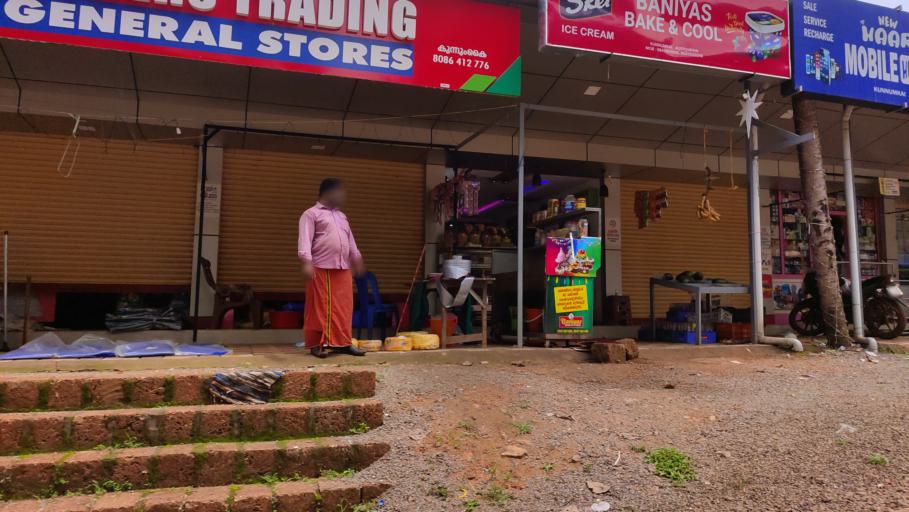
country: IN
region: Kerala
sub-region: Kasaragod District
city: Nileshwar
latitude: 12.2963
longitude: 75.2819
